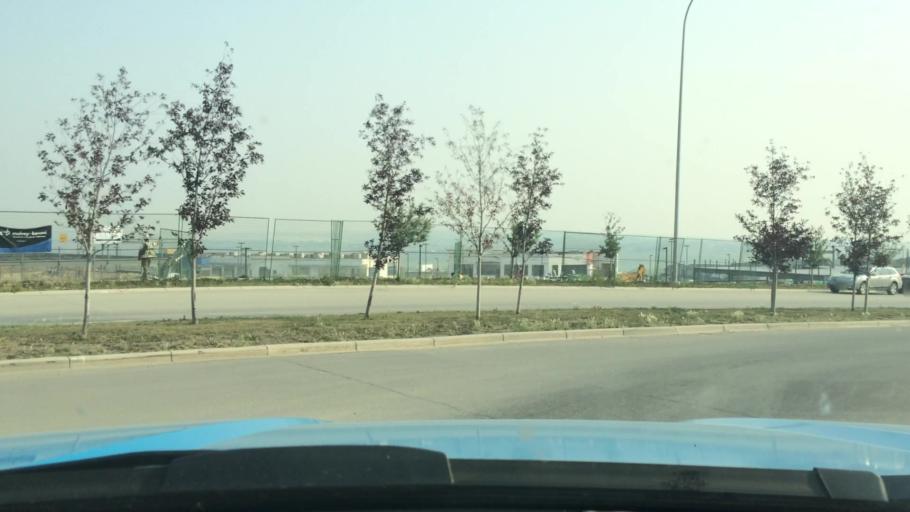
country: CA
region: Alberta
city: Calgary
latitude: 51.1800
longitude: -114.1597
